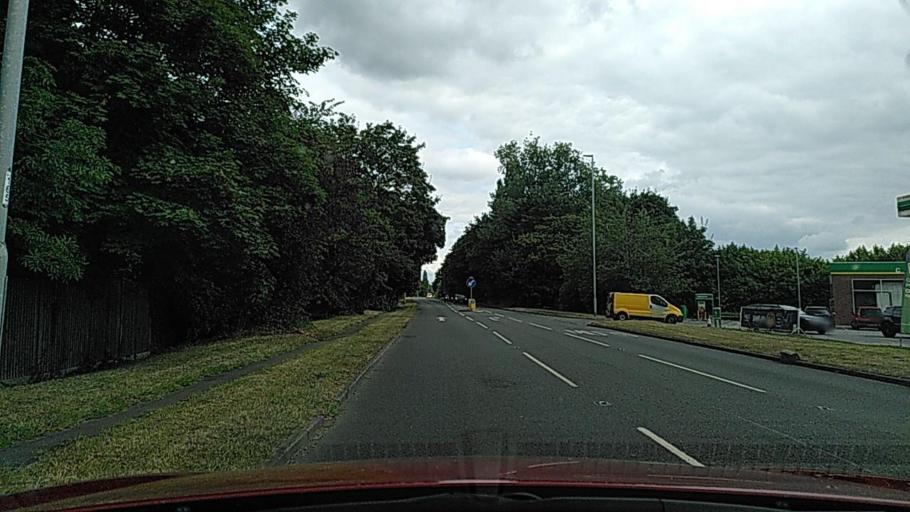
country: GB
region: England
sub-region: Wokingham
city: Wargrave
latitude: 51.4874
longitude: -0.8690
